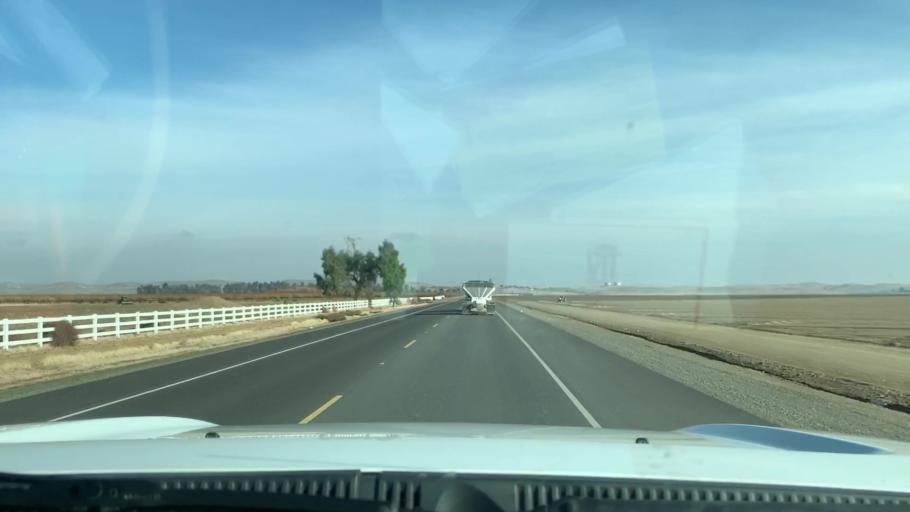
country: US
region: California
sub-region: Fresno County
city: Coalinga
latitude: 36.1847
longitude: -120.3491
